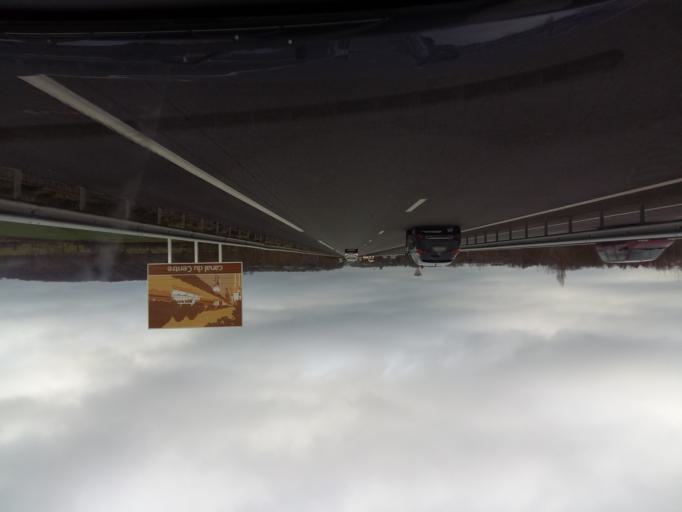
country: FR
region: Bourgogne
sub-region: Departement de Saone-et-Loire
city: Digoin
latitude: 46.4641
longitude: 3.9833
